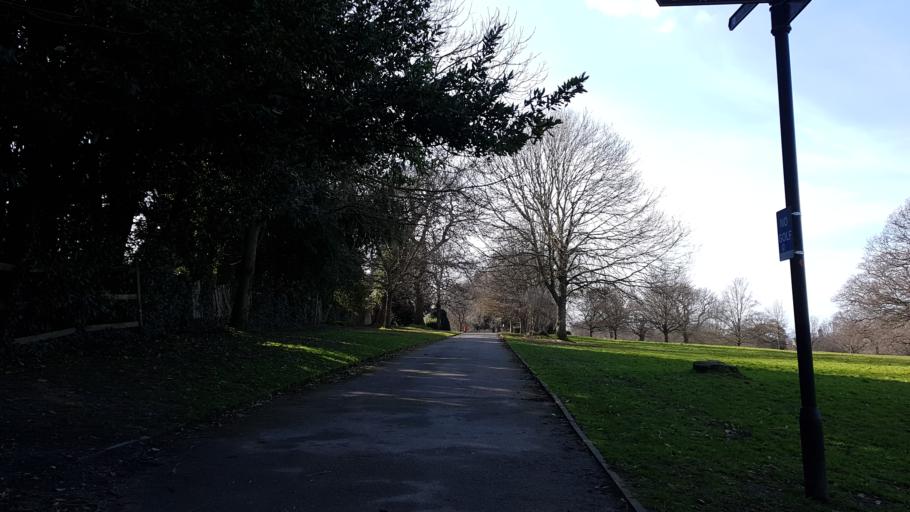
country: GB
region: England
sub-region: Isle of Wight
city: Ryde
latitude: 50.7249
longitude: -1.1388
